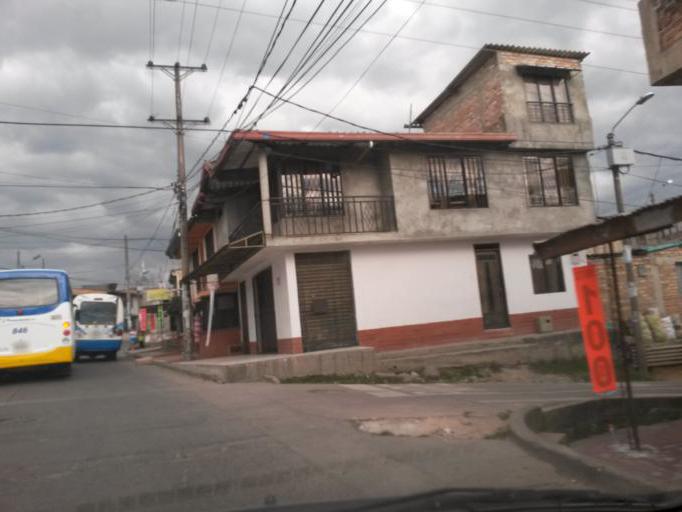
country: CO
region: Cauca
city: Popayan
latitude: 2.4471
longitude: -76.6290
